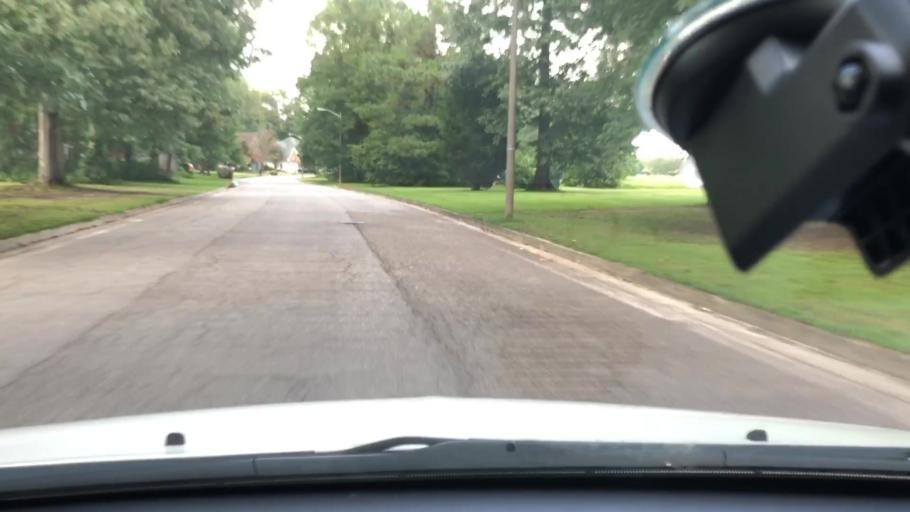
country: US
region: Virginia
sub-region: City of Chesapeake
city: Chesapeake
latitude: 36.7027
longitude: -76.2895
